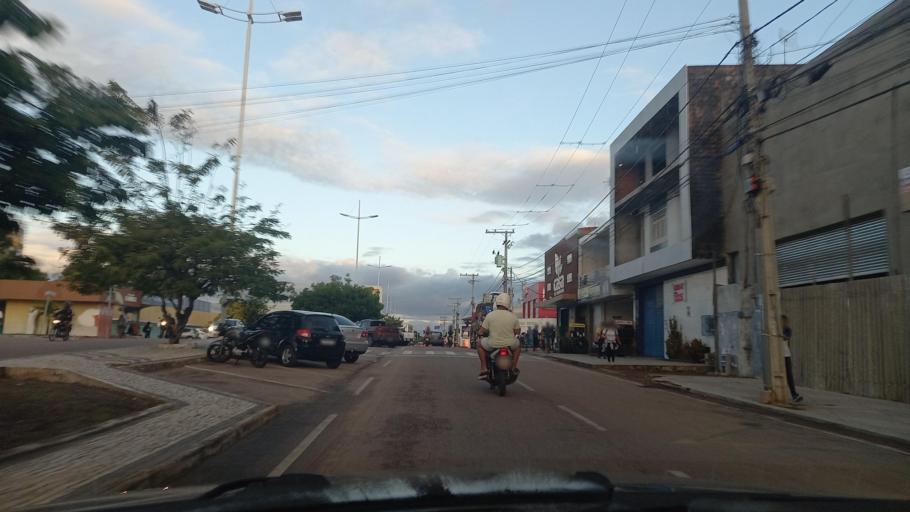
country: BR
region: Bahia
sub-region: Paulo Afonso
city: Paulo Afonso
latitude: -9.4005
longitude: -38.2317
